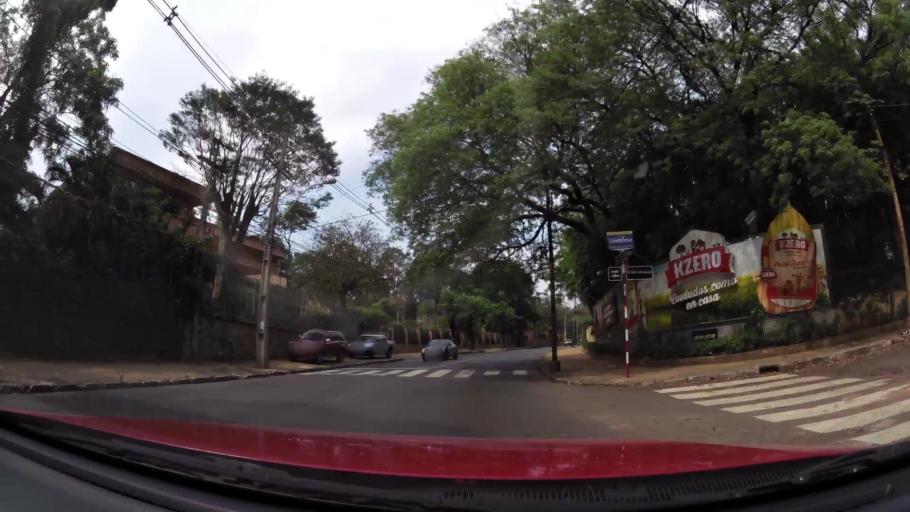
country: PY
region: Asuncion
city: Asuncion
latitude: -25.2854
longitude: -57.5823
